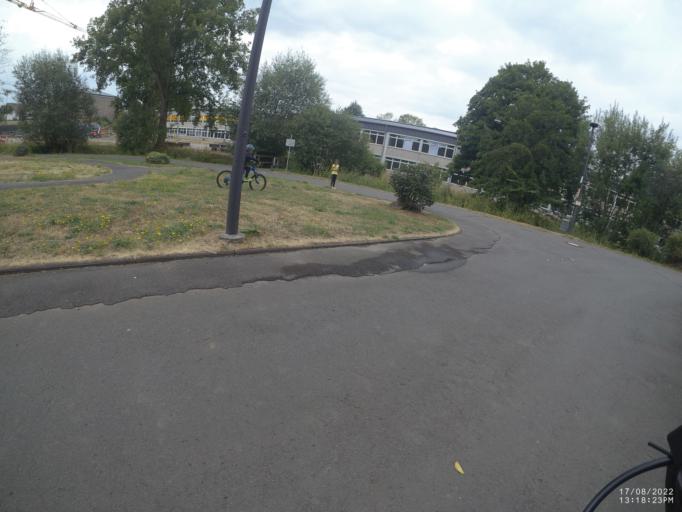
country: DE
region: Rheinland-Pfalz
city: Hillesheim
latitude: 50.2902
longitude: 6.6691
